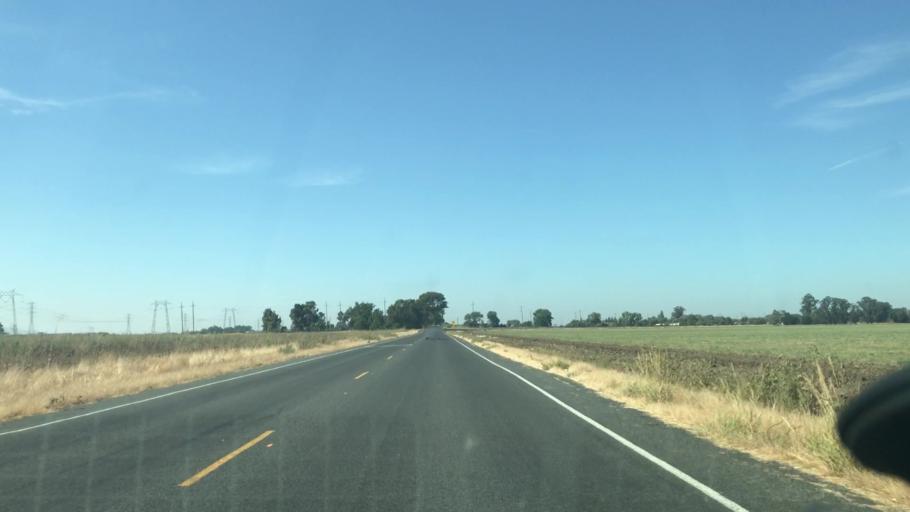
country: US
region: California
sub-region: Solano County
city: Vacaville
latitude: 38.3389
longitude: -121.9154
